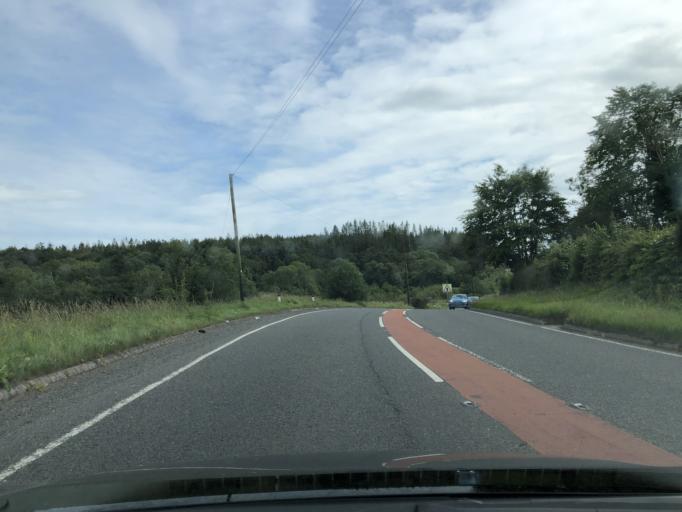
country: GB
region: Northern Ireland
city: Ballynahinch
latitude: 54.3522
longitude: -5.8526
